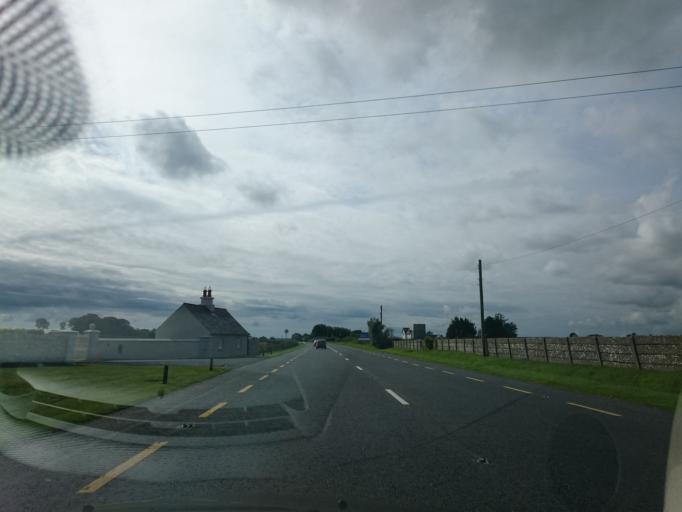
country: IE
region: Leinster
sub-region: Kilkenny
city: Kilkenny
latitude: 52.5887
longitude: -7.2409
